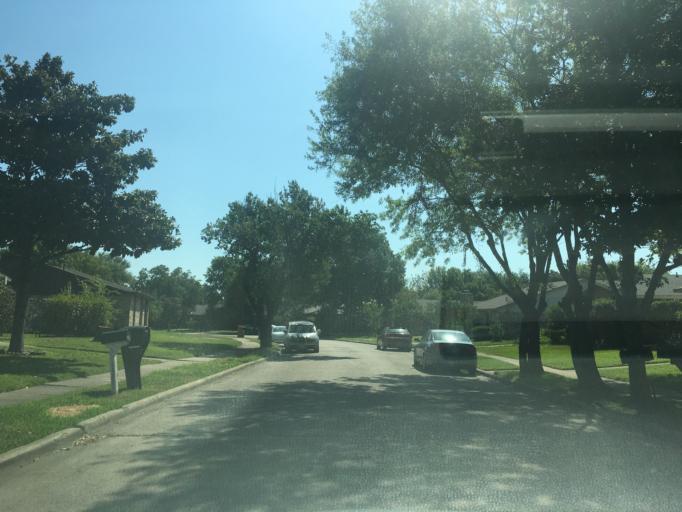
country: US
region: Texas
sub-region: Dallas County
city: Garland
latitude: 32.8532
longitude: -96.6606
